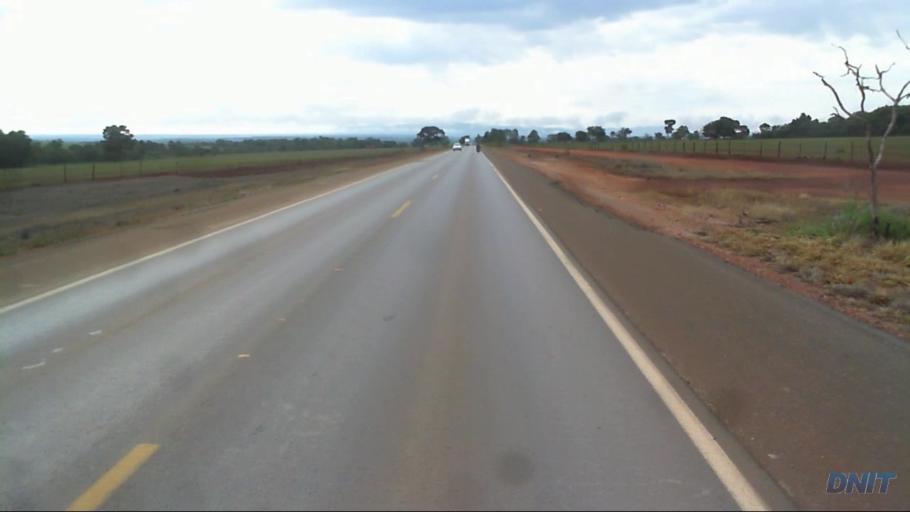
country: BR
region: Goias
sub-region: Uruacu
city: Uruacu
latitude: -14.7037
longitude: -49.1156
